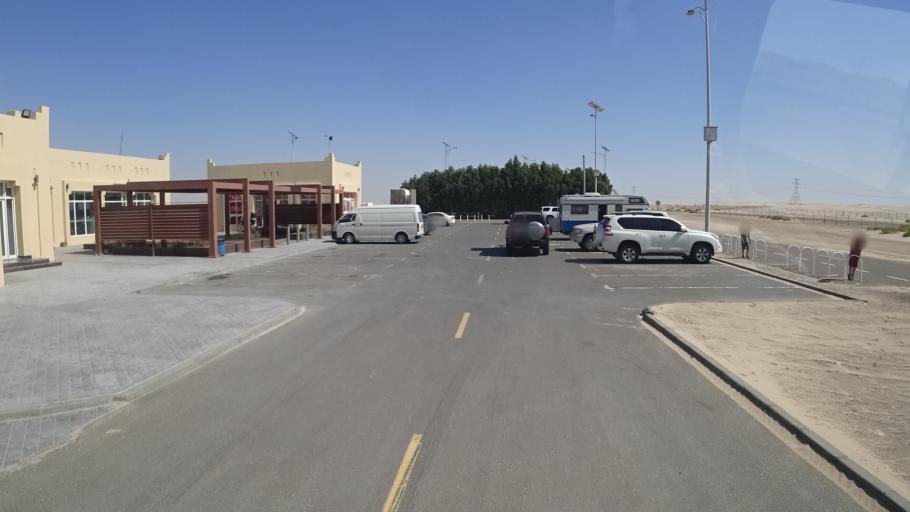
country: AE
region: Abu Dhabi
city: Abu Dhabi
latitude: 24.1609
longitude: 54.7470
